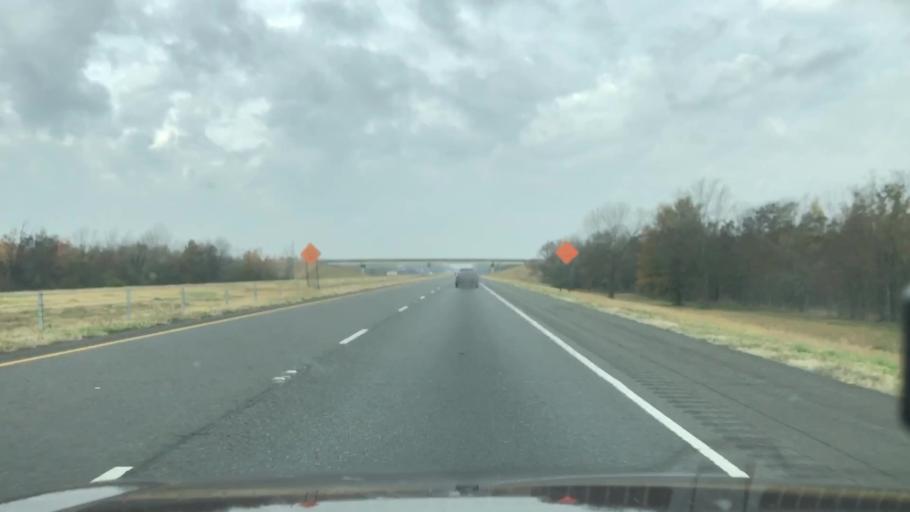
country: US
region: Louisiana
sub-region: Richland Parish
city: Delhi
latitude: 32.4369
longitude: -91.4544
